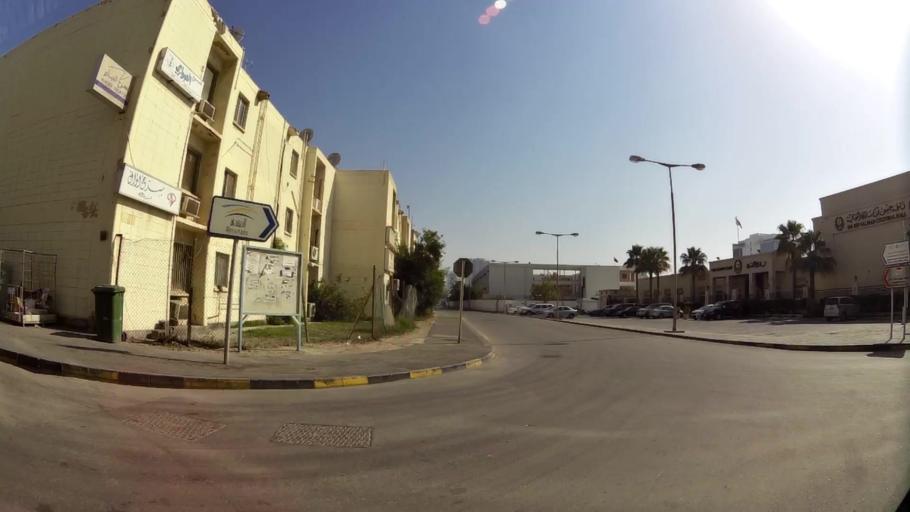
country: BH
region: Manama
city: Manama
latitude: 26.2097
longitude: 50.5905
